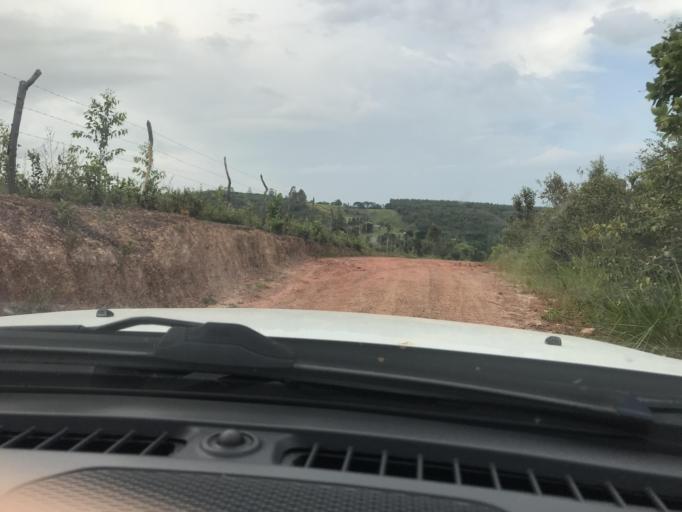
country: BR
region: Bahia
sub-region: Entre Rios
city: Entre Rios
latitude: -12.0144
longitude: -38.2213
